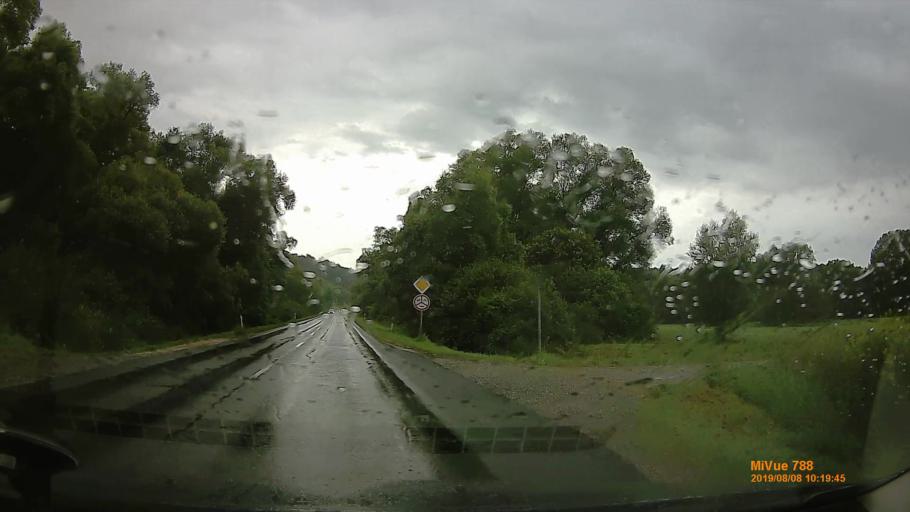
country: HU
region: Zala
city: Zalaegerszeg
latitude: 46.7606
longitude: 16.8577
